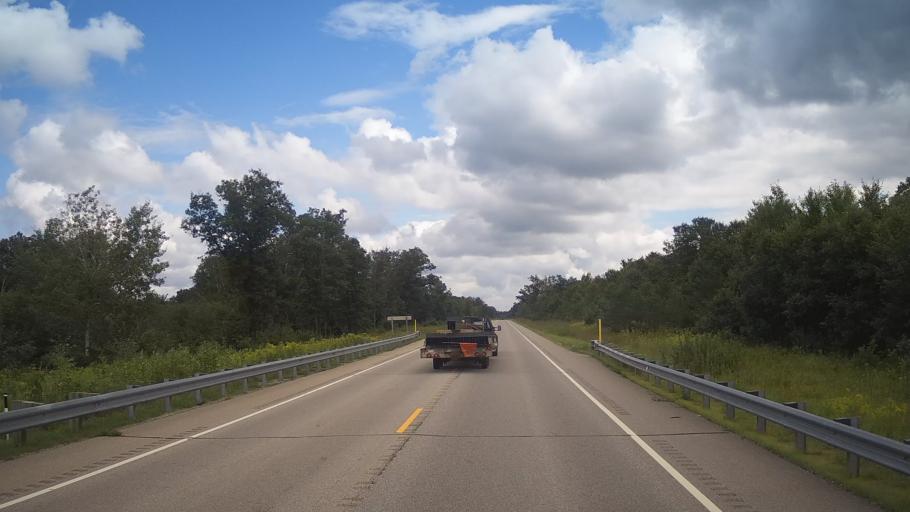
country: US
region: Wisconsin
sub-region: Adams County
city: Friendship
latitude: 44.0256
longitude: -89.7079
